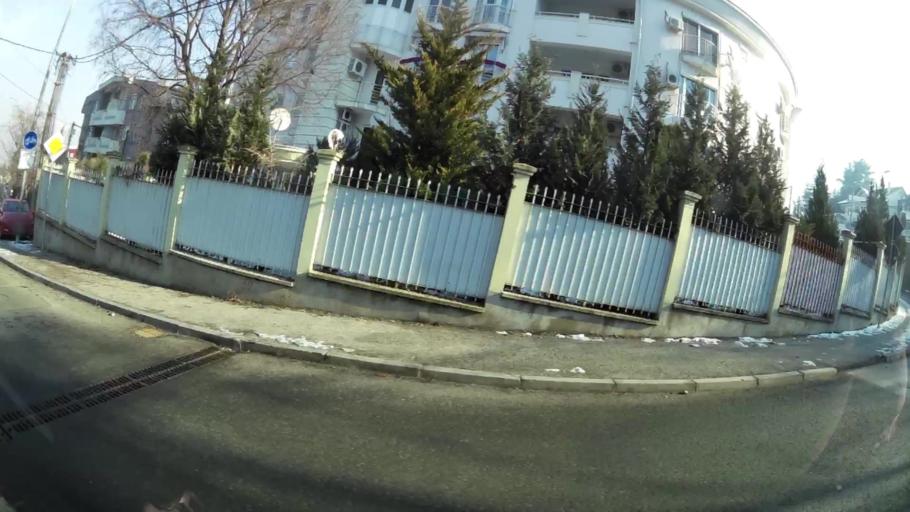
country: MK
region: Karpos
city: Skopje
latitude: 41.9835
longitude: 21.4188
